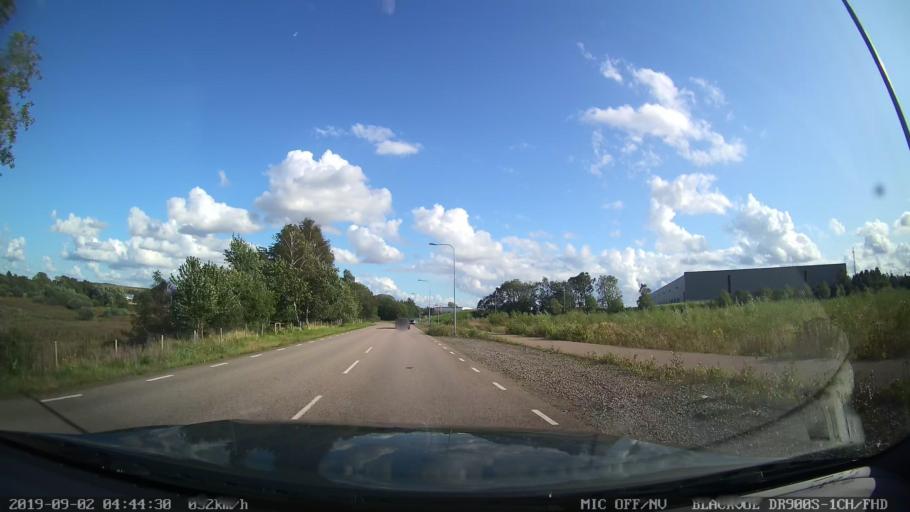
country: SE
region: Skane
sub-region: Helsingborg
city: Odakra
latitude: 56.0773
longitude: 12.7450
